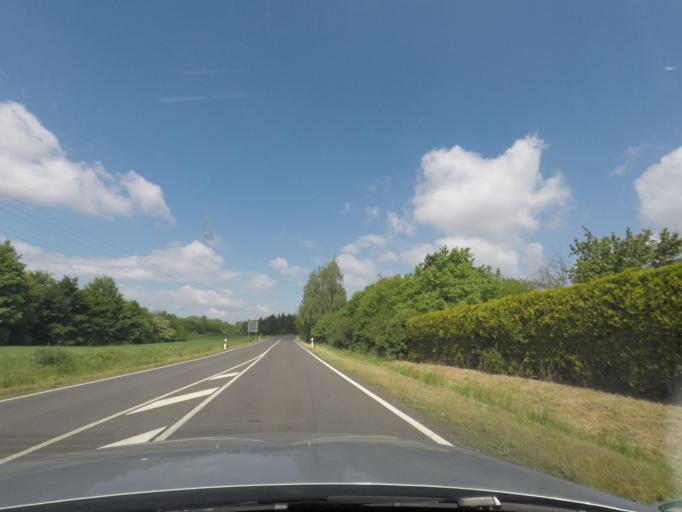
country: DE
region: Saxony
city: Bohlen
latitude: 51.1717
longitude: 12.3745
